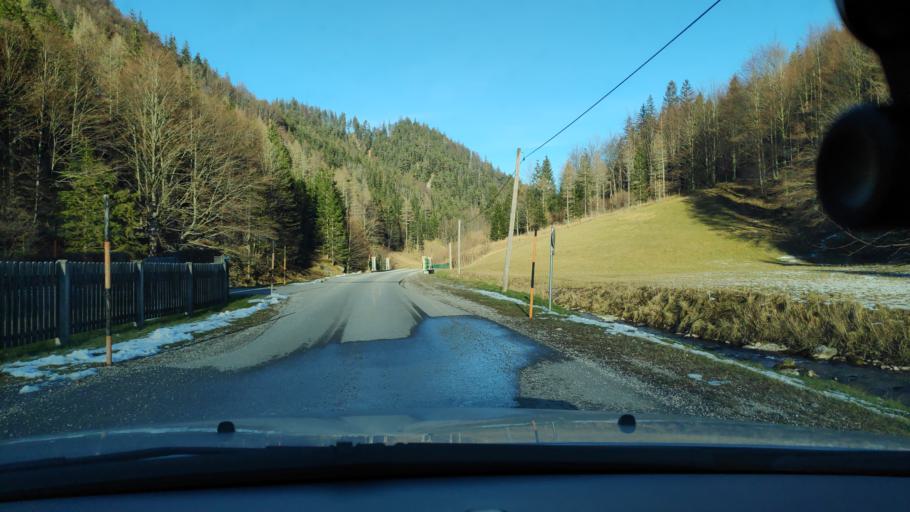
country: AT
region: Lower Austria
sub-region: Politischer Bezirk Neunkirchen
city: Schwarzau im Gebirge
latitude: 47.7425
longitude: 15.6719
